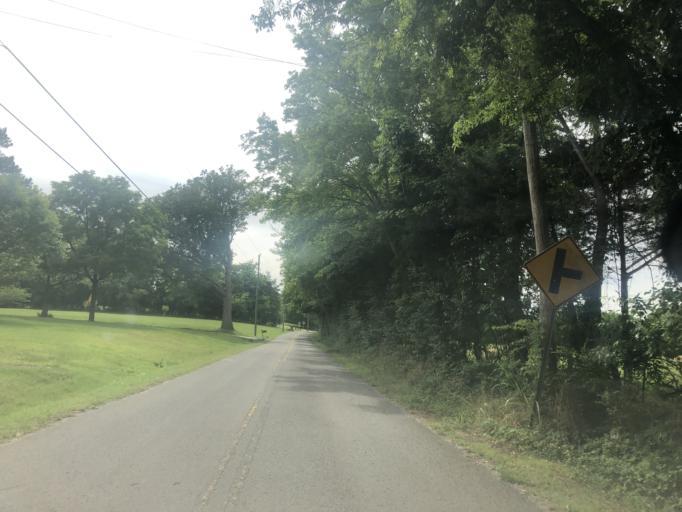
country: US
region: Tennessee
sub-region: Davidson County
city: Lakewood
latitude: 36.2173
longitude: -86.6509
